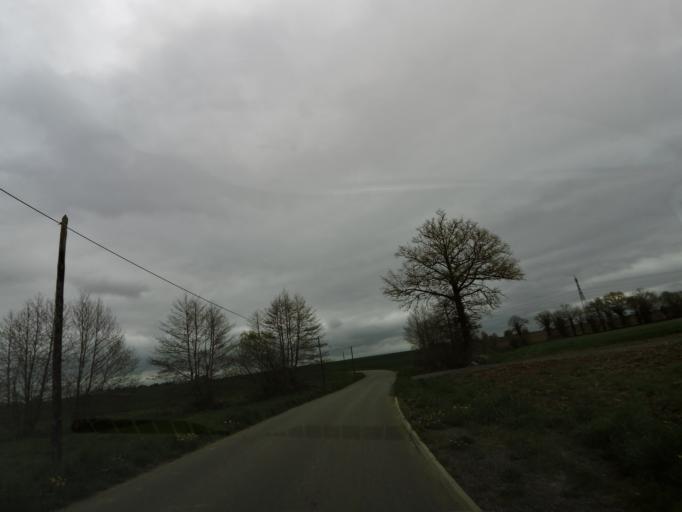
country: FR
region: Brittany
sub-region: Departement d'Ille-et-Vilaine
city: Janze
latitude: 47.9830
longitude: -1.5308
